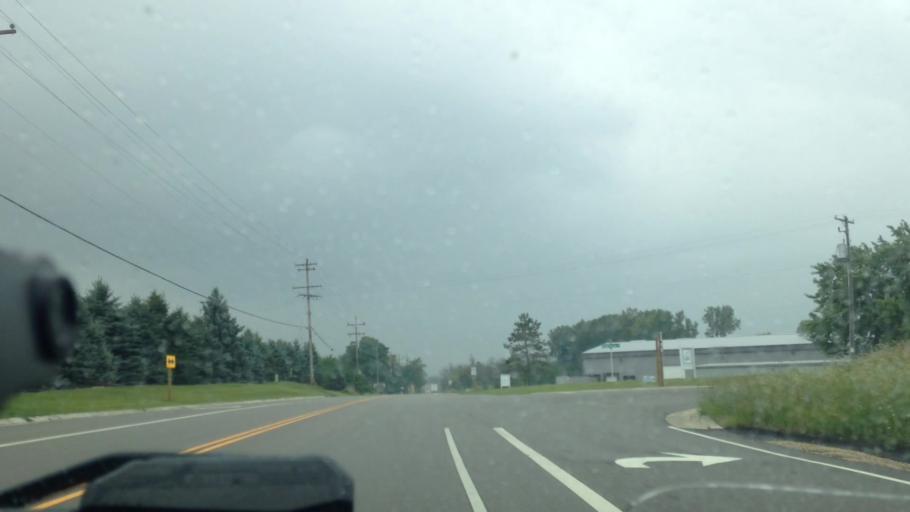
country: US
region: Wisconsin
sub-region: Washington County
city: Richfield
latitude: 43.2951
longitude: -88.2209
